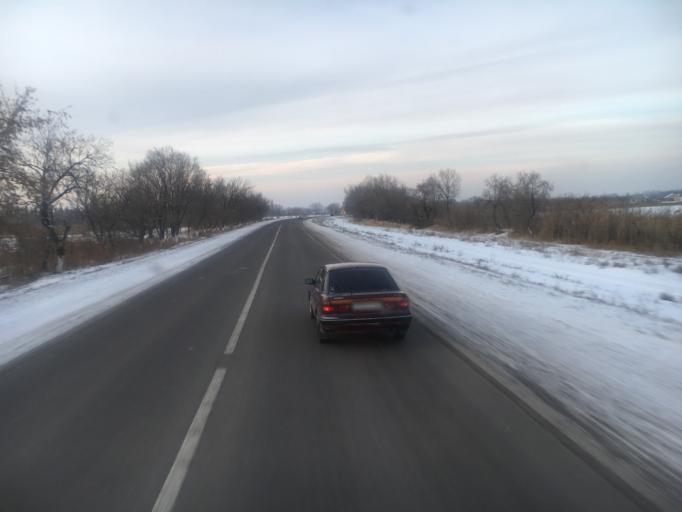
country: KZ
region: Almaty Oblysy
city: Burunday
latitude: 43.3520
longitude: 76.6484
